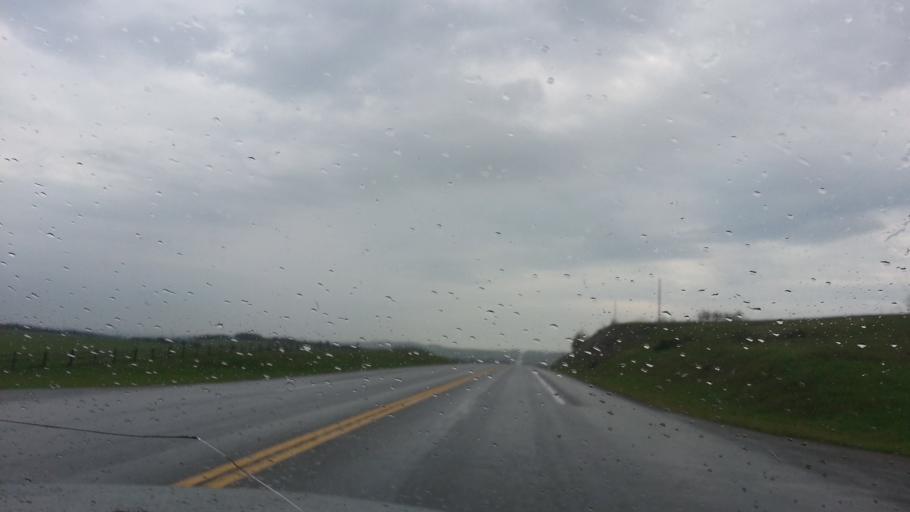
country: CA
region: Alberta
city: Cochrane
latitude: 51.0541
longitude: -114.4667
